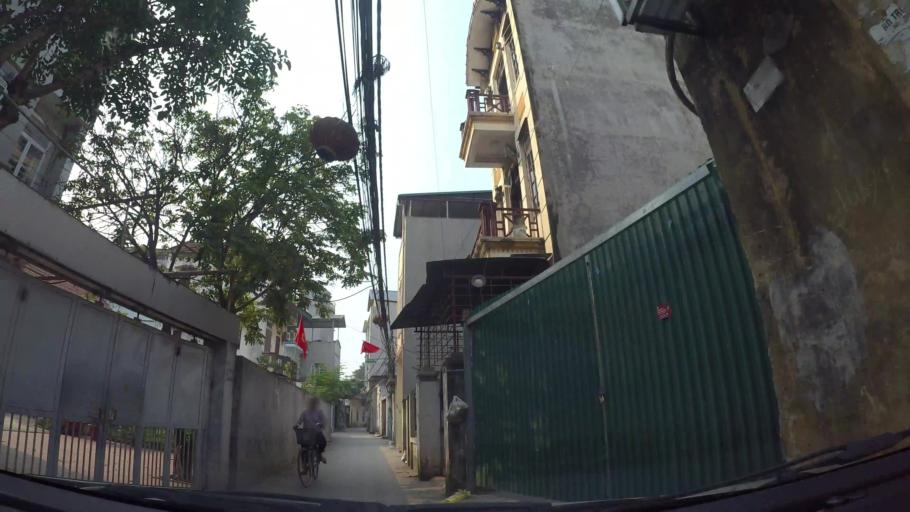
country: VN
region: Ha Noi
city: Ha Dong
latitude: 20.9950
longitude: 105.7530
